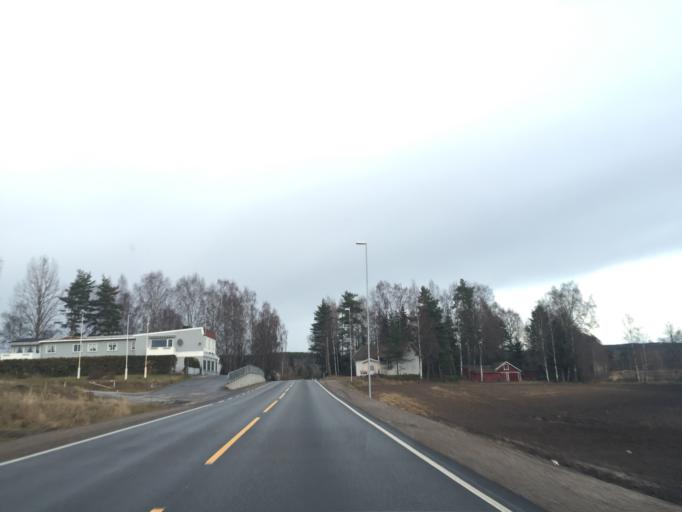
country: NO
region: Hedmark
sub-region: Grue
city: Kirkenaer
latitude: 60.5427
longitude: 12.0603
